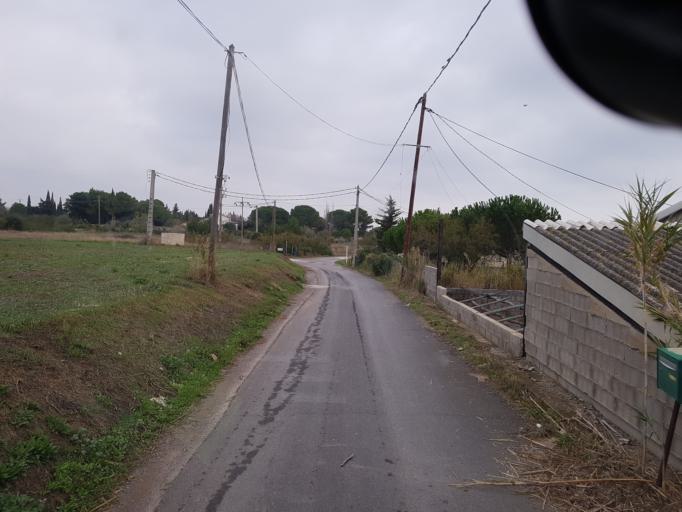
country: FR
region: Languedoc-Roussillon
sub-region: Departement de l'Herault
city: Marseillan
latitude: 43.3673
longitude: 3.5391
